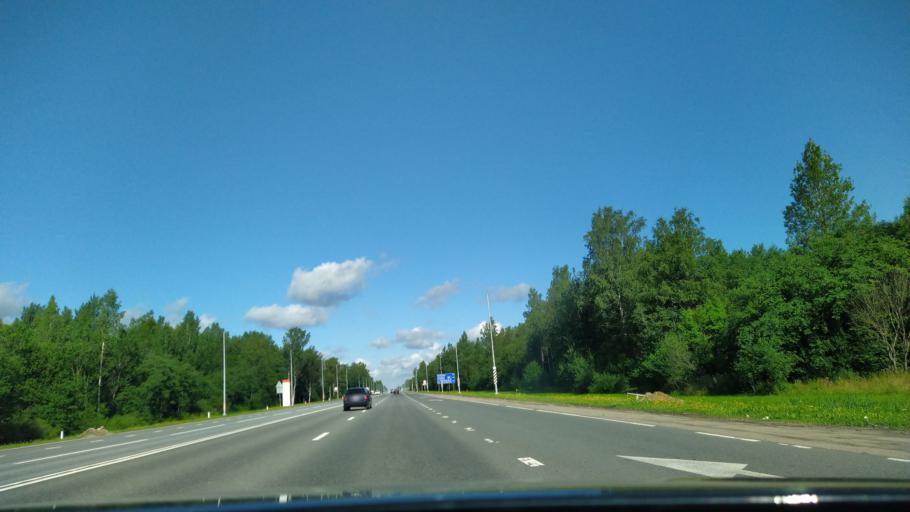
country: RU
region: Leningrad
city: Tosno
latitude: 59.5722
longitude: 30.8203
